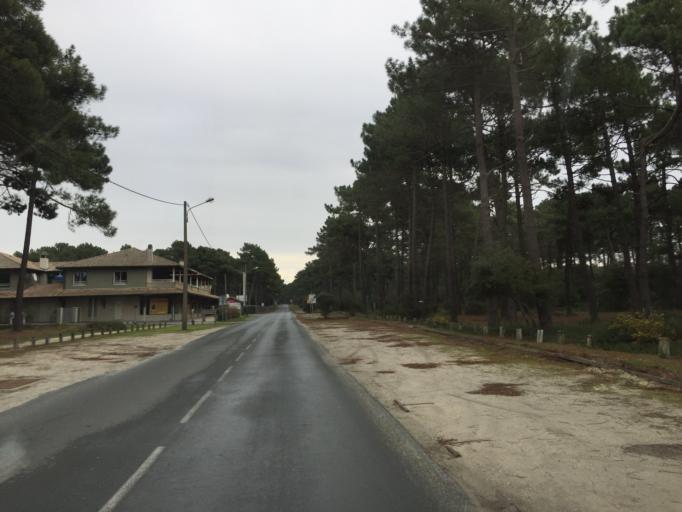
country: FR
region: Aquitaine
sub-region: Departement de la Gironde
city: Hourtin
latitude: 45.2229
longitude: -1.1663
